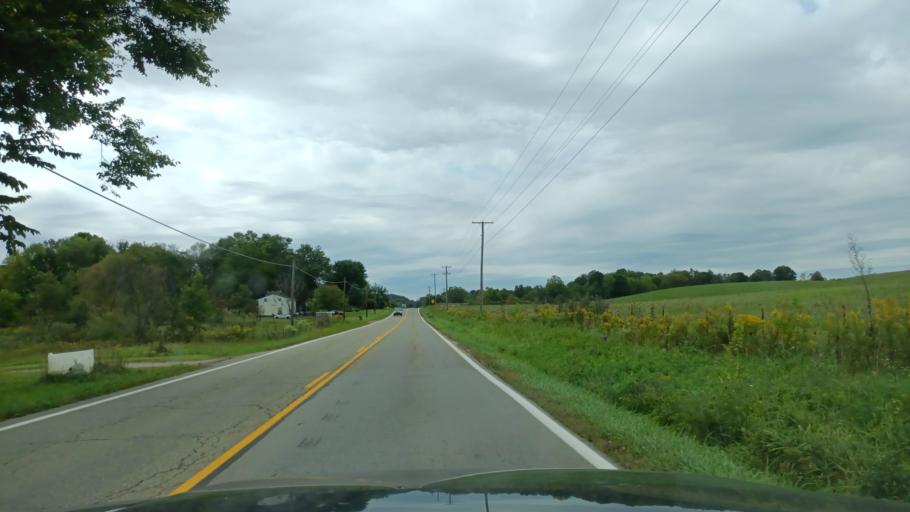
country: US
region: Ohio
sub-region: Vinton County
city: McArthur
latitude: 39.2574
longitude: -82.5002
